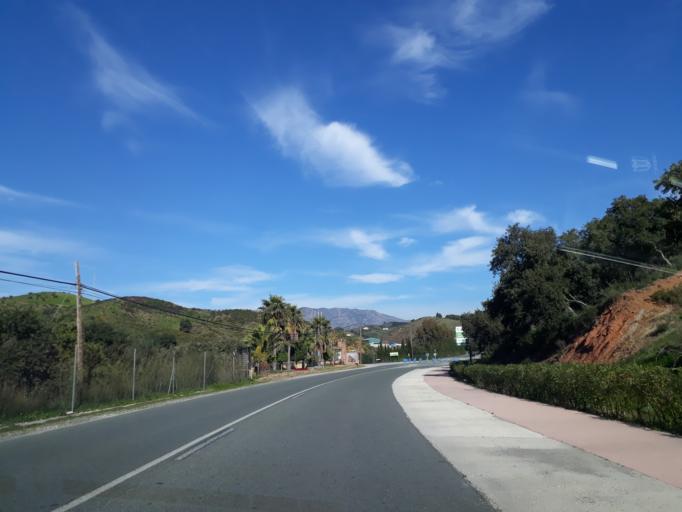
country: ES
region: Andalusia
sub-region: Provincia de Malaga
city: Fuengirola
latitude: 36.5140
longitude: -4.6869
